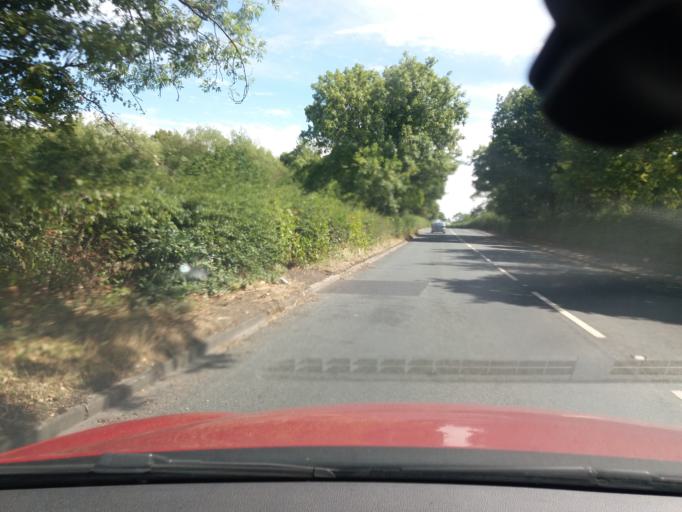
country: GB
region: England
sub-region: Lancashire
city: Euxton
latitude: 53.6613
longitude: -2.7052
